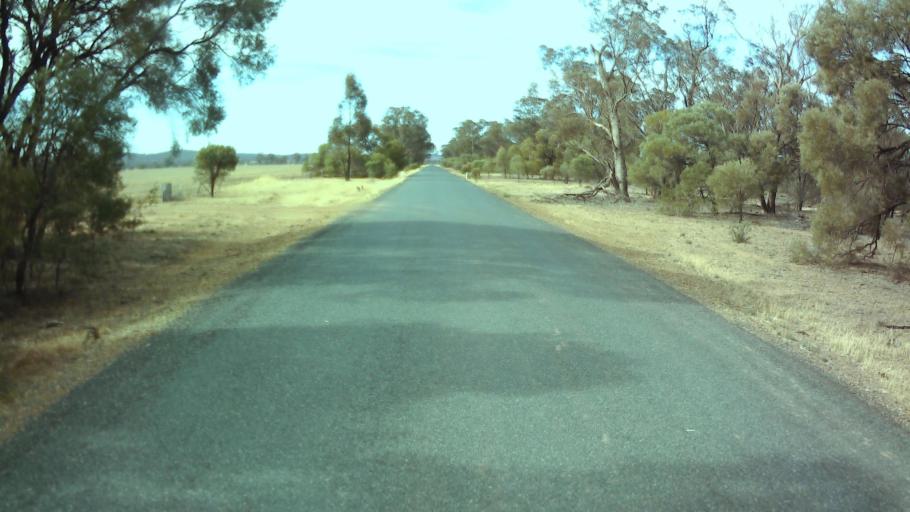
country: AU
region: New South Wales
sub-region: Weddin
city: Grenfell
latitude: -33.8663
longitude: 147.8589
